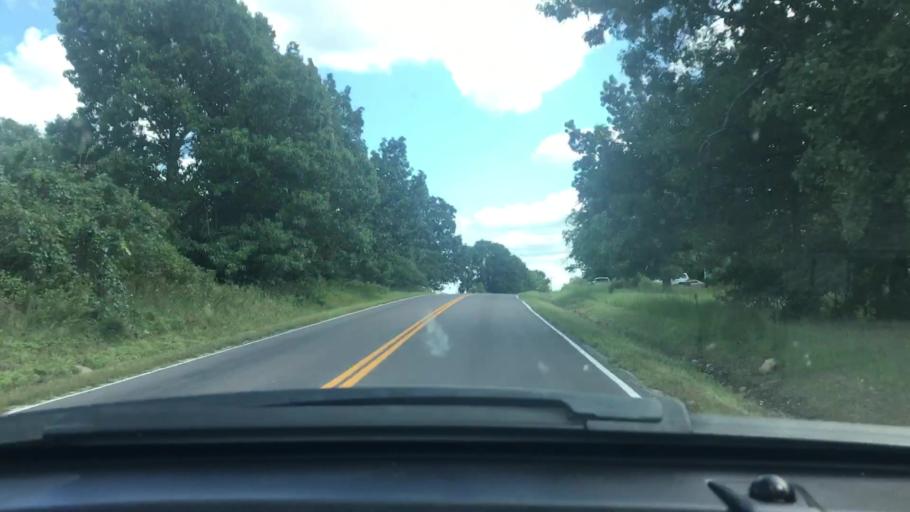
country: US
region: Missouri
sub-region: Wright County
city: Hartville
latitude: 37.3621
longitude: -92.3448
